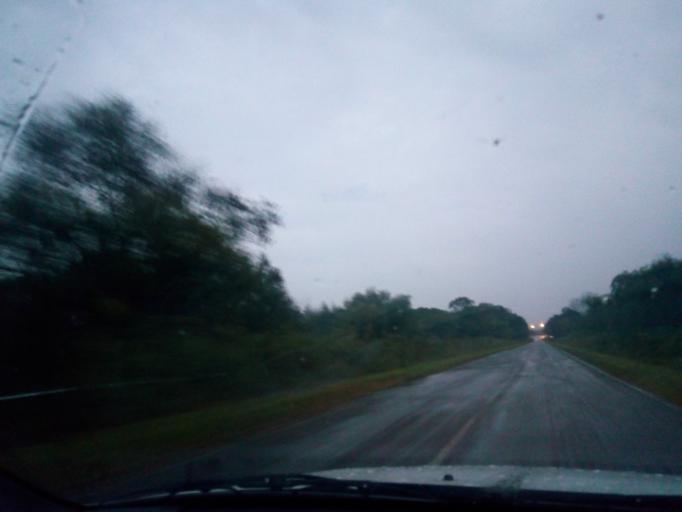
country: RU
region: Primorskiy
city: Lazo
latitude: 45.8701
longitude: 133.7138
